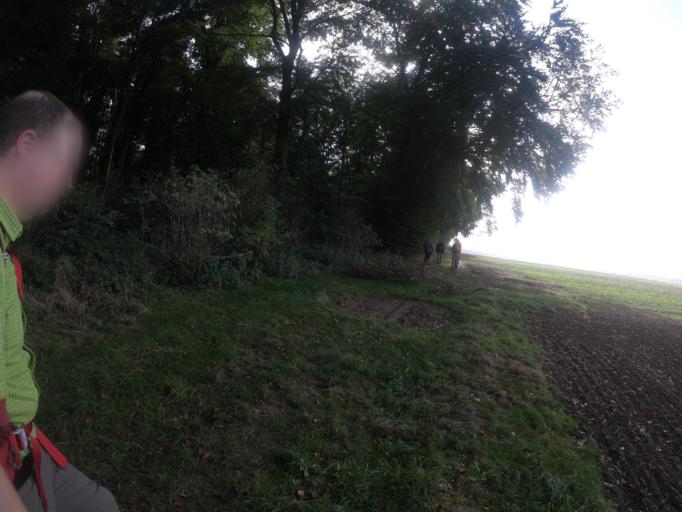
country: DE
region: Hesse
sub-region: Regierungsbezirk Giessen
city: Villmar
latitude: 50.3397
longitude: 8.2011
